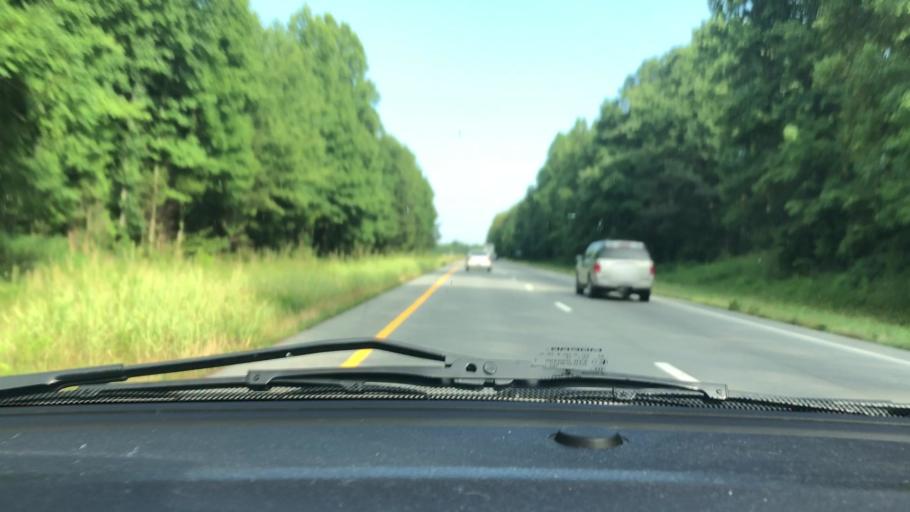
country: US
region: North Carolina
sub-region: Randolph County
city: Liberty
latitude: 35.8584
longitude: -79.6169
